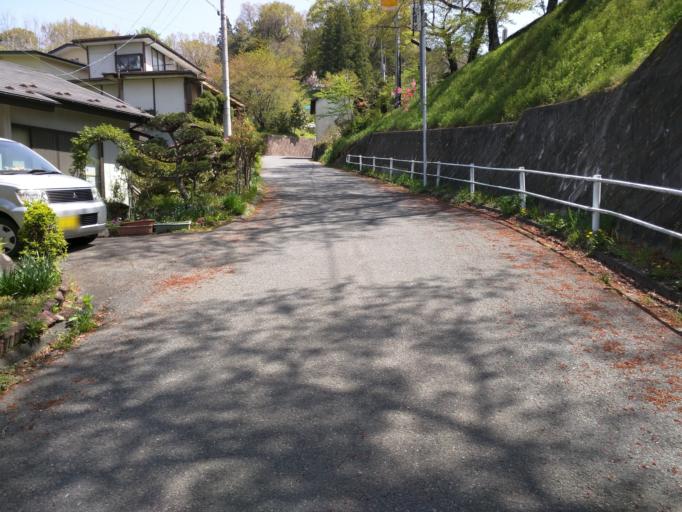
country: JP
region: Fukushima
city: Nihommatsu
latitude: 37.5624
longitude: 140.5087
